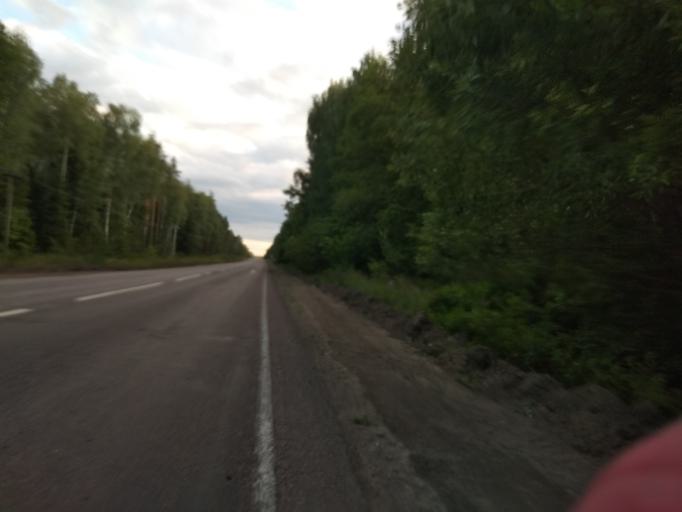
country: RU
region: Moskovskaya
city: Misheronskiy
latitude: 55.6415
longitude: 39.7541
